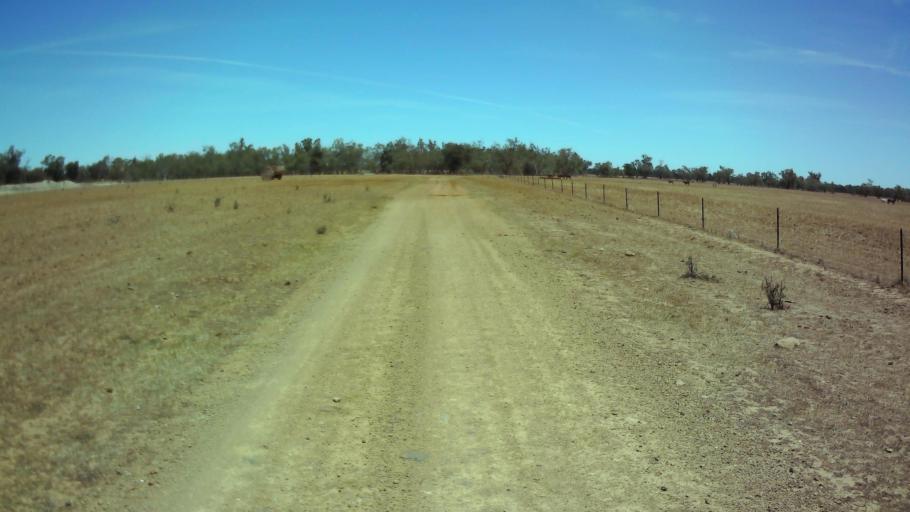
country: AU
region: New South Wales
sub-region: Bland
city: West Wyalong
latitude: -33.8300
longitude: 147.6368
